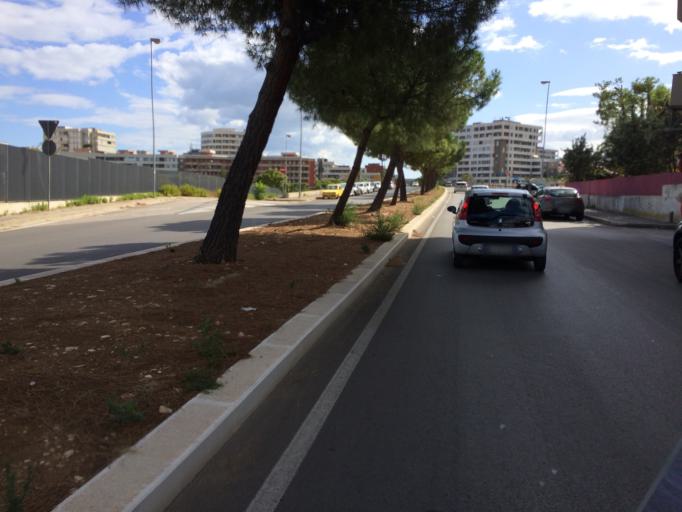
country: IT
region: Apulia
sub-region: Provincia di Bari
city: Bari
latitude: 41.0933
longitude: 16.8556
